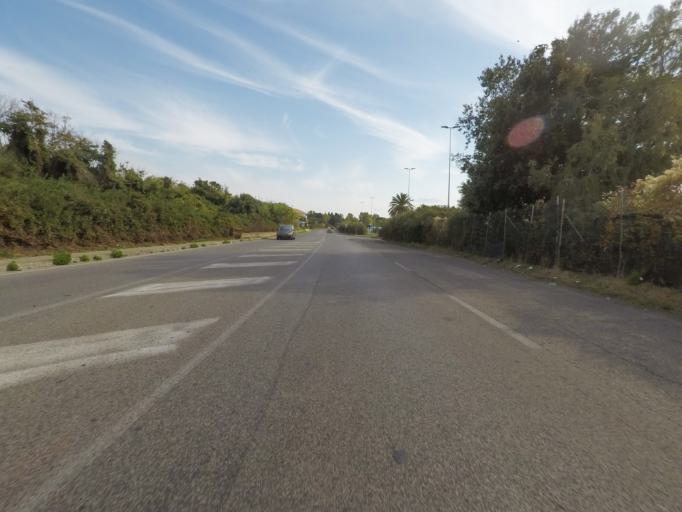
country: IT
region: Latium
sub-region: Citta metropolitana di Roma Capitale
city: Civitavecchia
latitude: 42.0623
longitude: 11.8154
